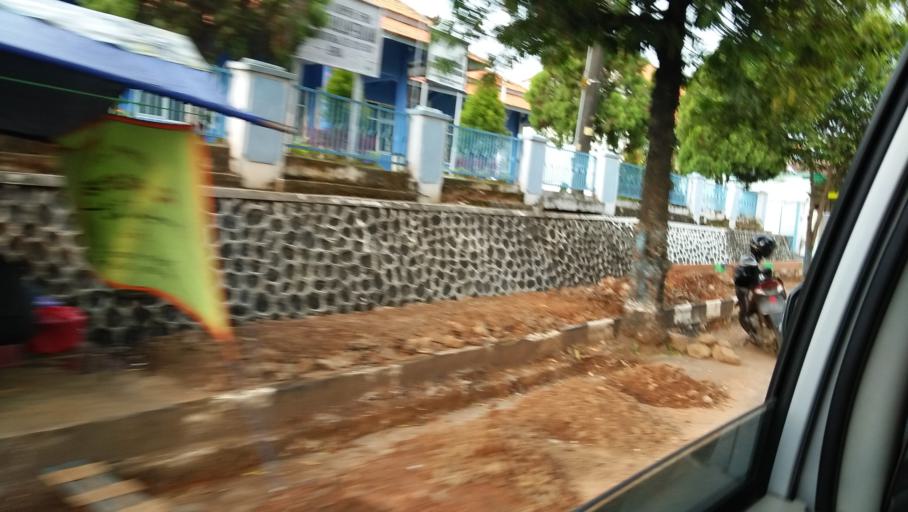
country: ID
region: Central Java
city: Mlonggo
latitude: -6.5895
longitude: 110.6763
